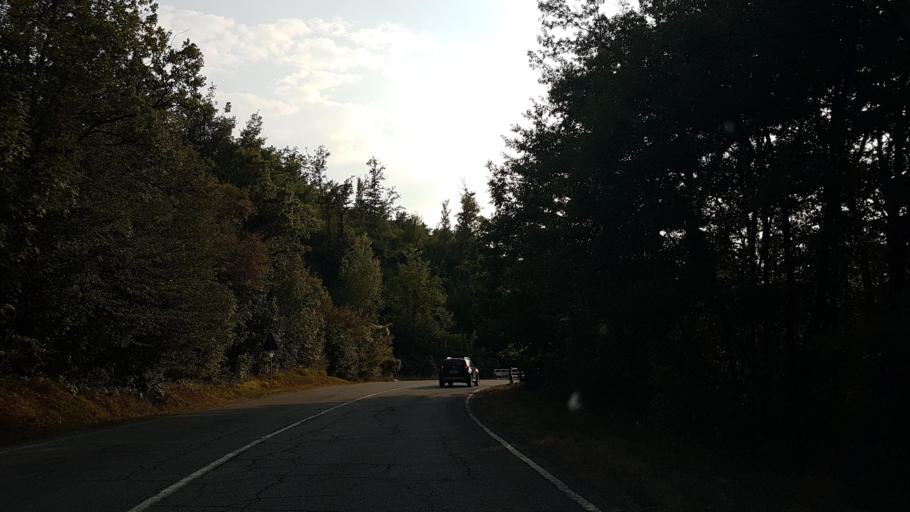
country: IT
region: Emilia-Romagna
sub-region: Provincia di Parma
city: Solignano
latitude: 44.6163
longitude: 9.9981
